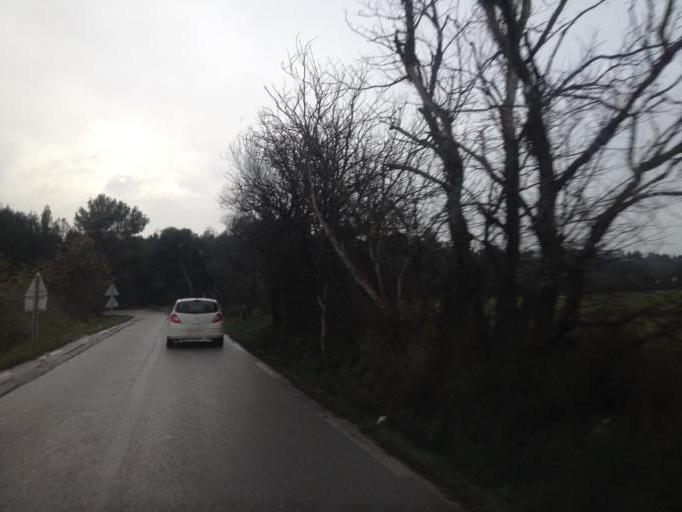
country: FR
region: Provence-Alpes-Cote d'Azur
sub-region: Departement des Bouches-du-Rhone
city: Cabries
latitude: 43.4991
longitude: 5.3499
